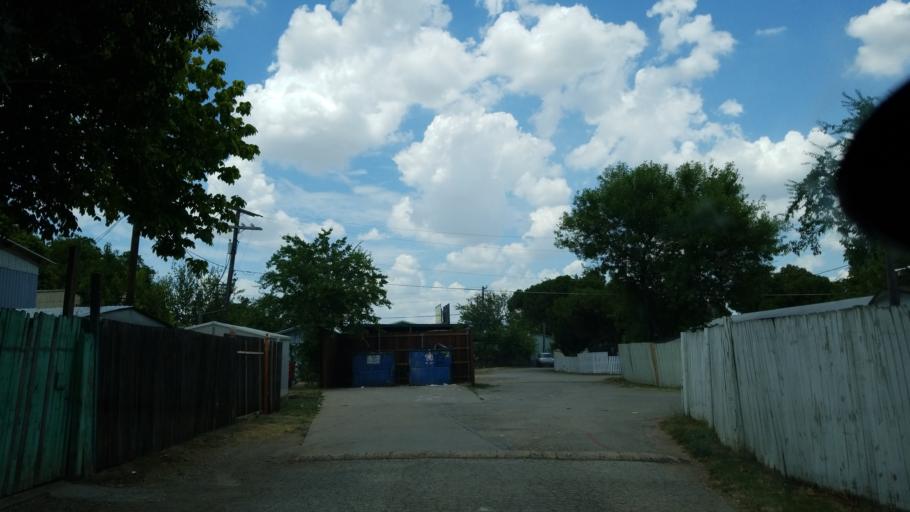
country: US
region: Texas
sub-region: Dallas County
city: Cockrell Hill
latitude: 32.7483
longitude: -96.8865
